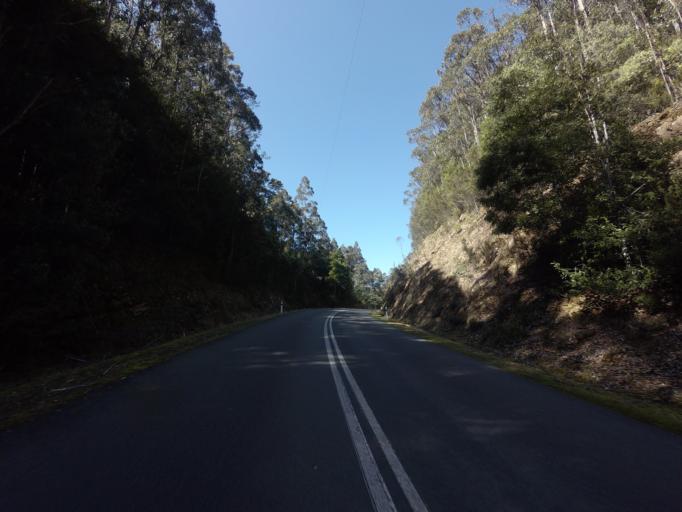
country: AU
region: Tasmania
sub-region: Derwent Valley
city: New Norfolk
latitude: -42.7438
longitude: 146.5004
